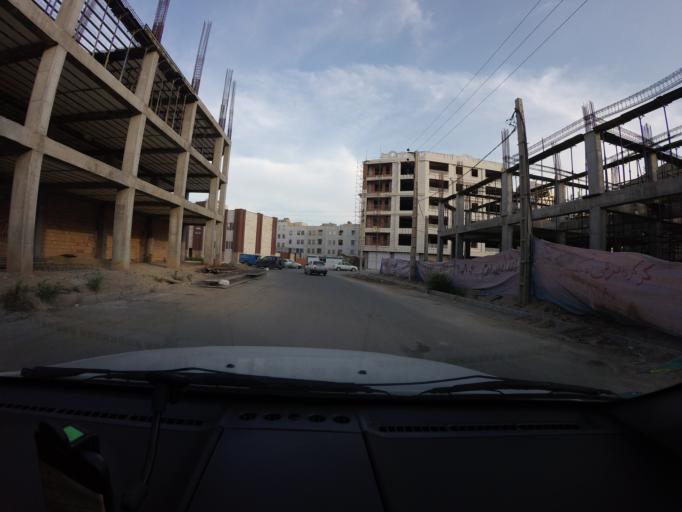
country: IR
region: Tehran
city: Eslamshahr
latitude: 35.5260
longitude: 51.2217
